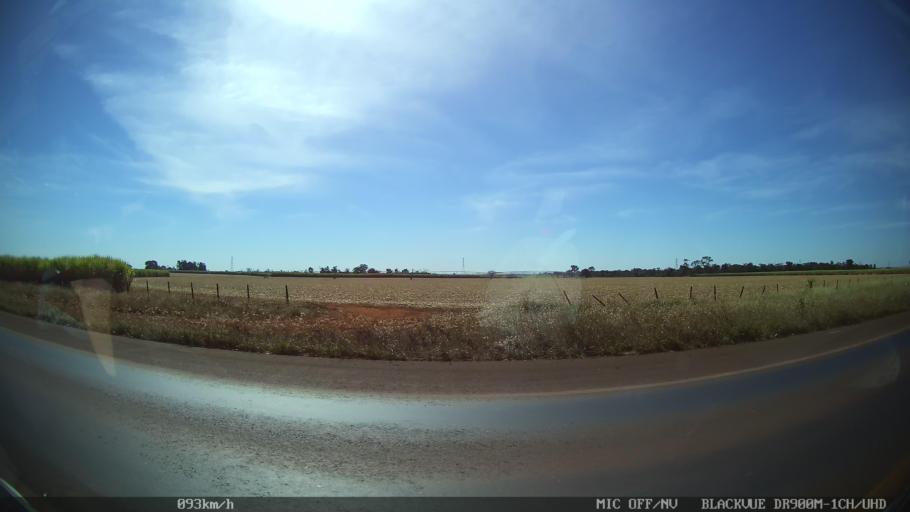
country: BR
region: Sao Paulo
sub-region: Ipua
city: Ipua
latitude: -20.5046
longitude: -47.9343
